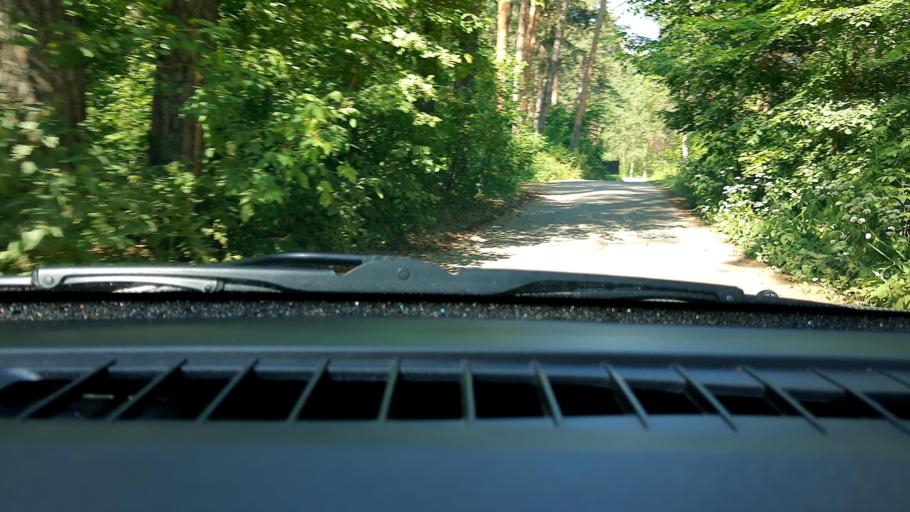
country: RU
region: Nizjnij Novgorod
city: Burevestnik
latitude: 56.1955
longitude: 43.8014
